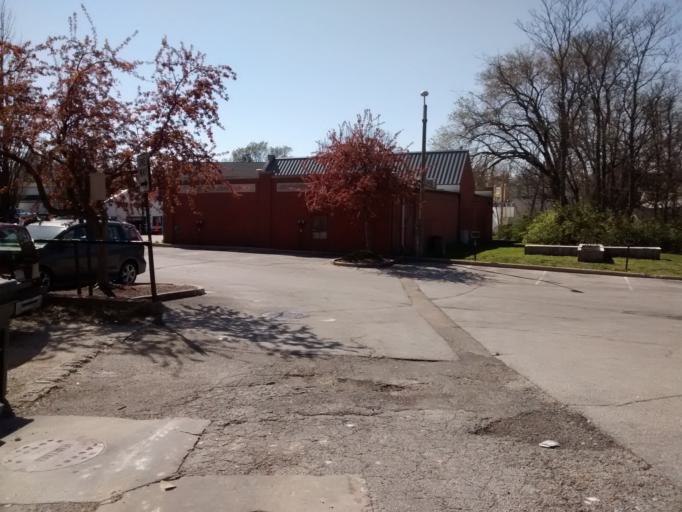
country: US
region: Illinois
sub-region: Champaign County
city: Urbana
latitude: 40.1129
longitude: -88.2098
